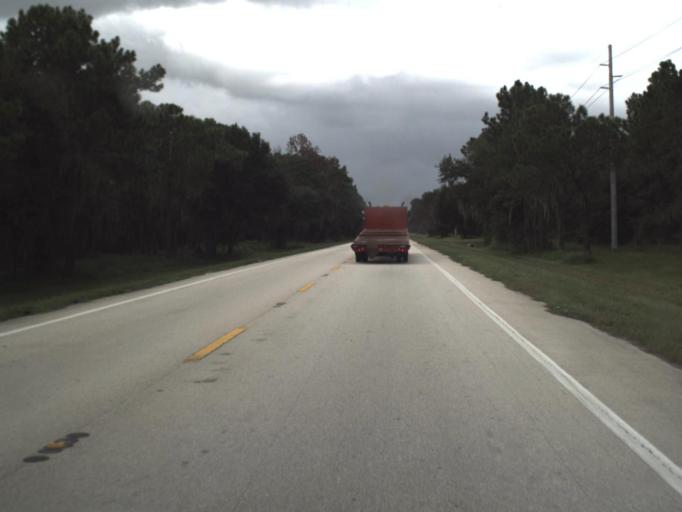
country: US
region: Florida
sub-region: Polk County
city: Mulberry
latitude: 27.7128
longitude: -82.0155
